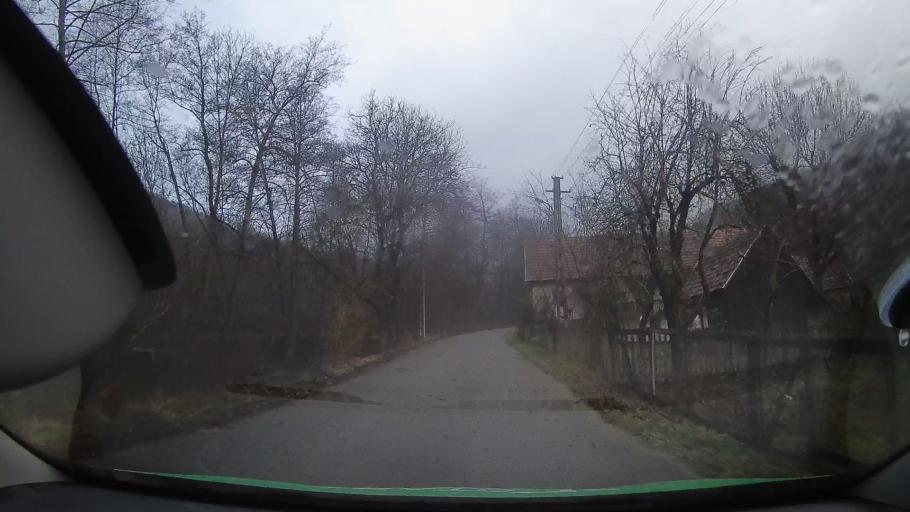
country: RO
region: Hunedoara
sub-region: Comuna Ribita
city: Ribita
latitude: 46.2522
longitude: 22.7504
